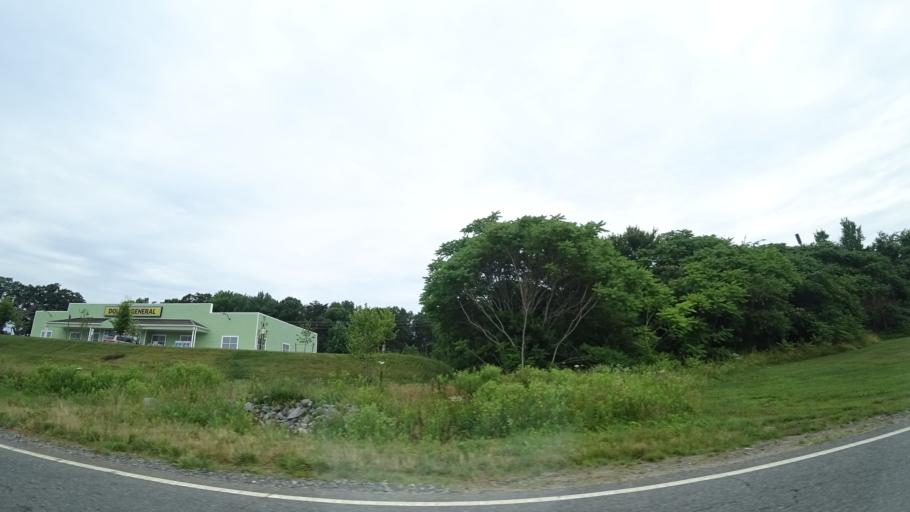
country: US
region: Virginia
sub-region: Spotsylvania County
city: Spotsylvania Courthouse
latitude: 38.1174
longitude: -77.7639
